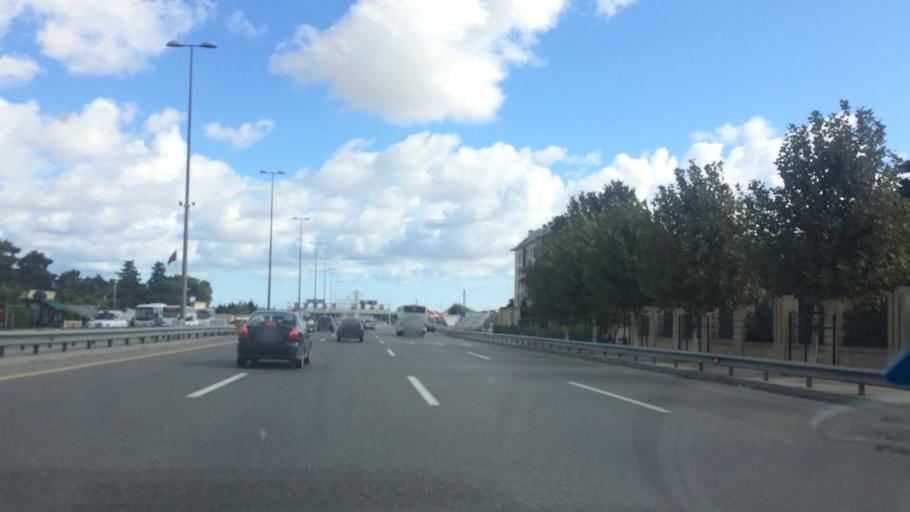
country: AZ
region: Baki
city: Biny Selo
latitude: 40.4549
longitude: 50.0676
